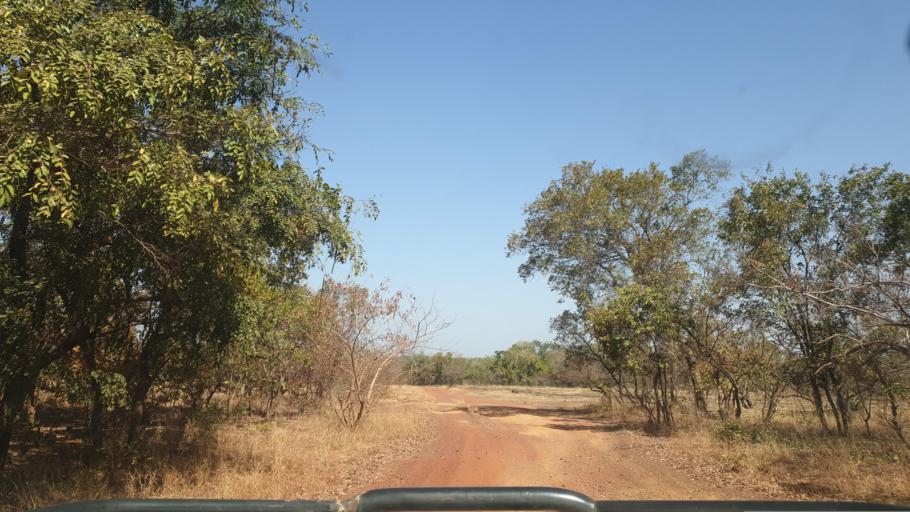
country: ML
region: Koulikoro
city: Dioila
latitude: 11.9198
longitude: -6.9838
